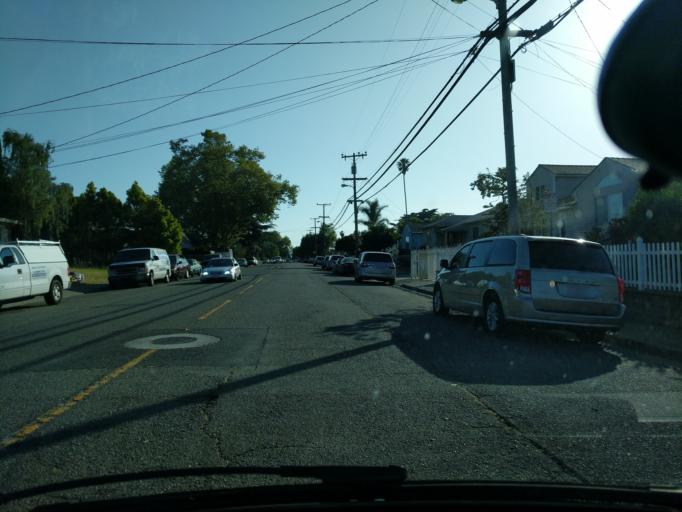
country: US
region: California
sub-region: Alameda County
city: San Leandro
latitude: 37.7040
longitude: -122.1825
